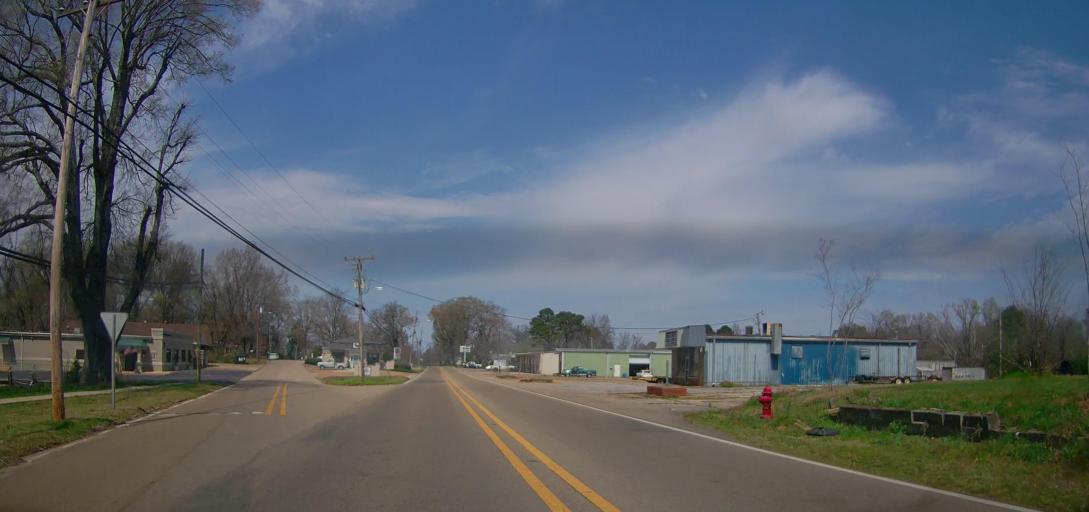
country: US
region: Mississippi
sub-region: Union County
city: New Albany
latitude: 34.4869
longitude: -89.0021
